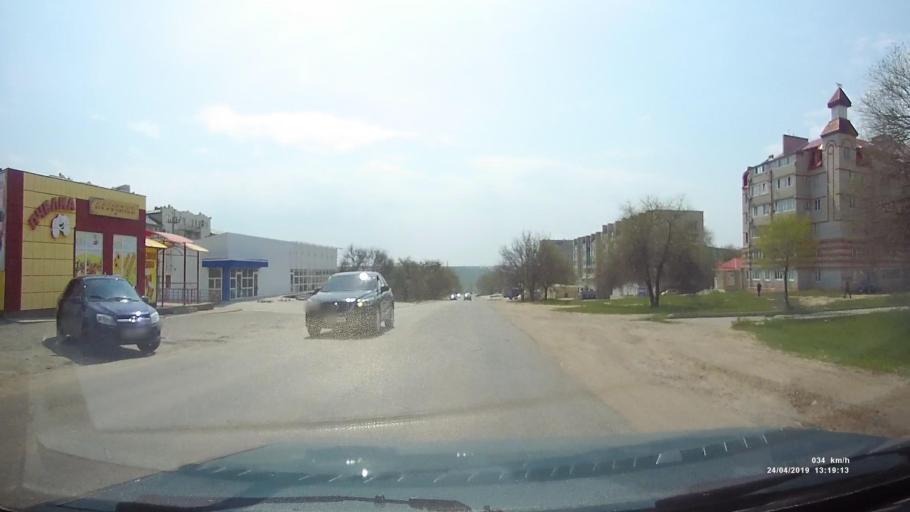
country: RU
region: Kalmykiya
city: Elista
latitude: 46.3009
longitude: 44.2921
